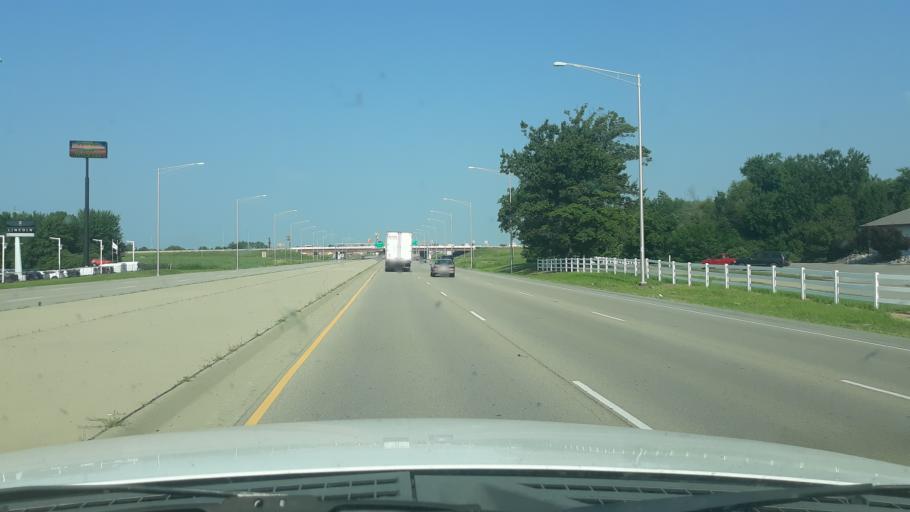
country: US
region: Illinois
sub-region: Williamson County
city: Marion
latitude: 37.7407
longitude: -88.9516
